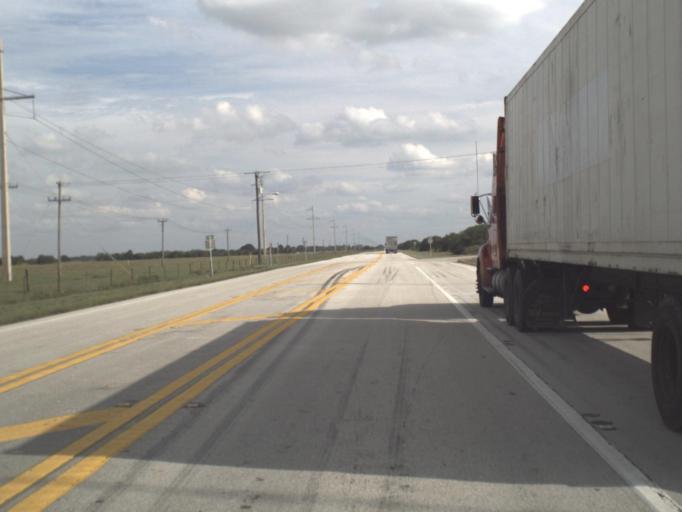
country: US
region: Florida
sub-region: Okeechobee County
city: Taylor Creek
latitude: 27.1944
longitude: -80.7307
